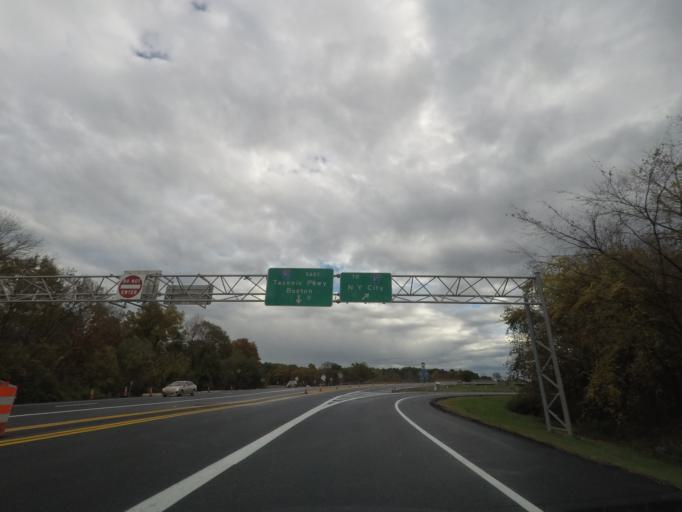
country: US
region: New York
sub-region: Columbia County
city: Niverville
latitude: 42.4845
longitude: -73.6712
